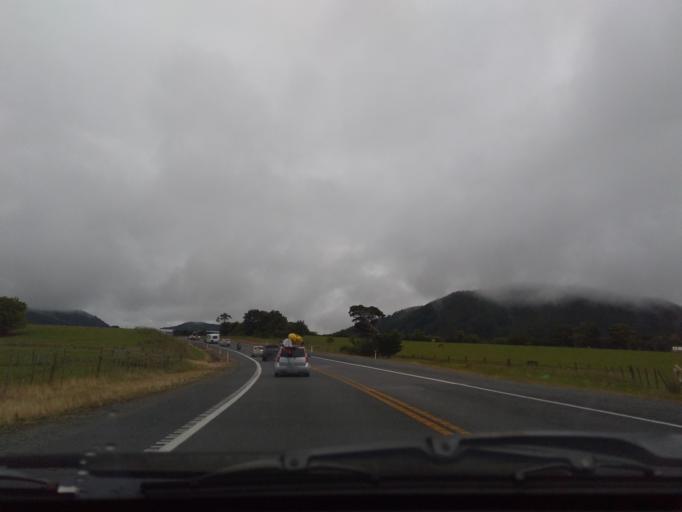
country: NZ
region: Auckland
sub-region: Auckland
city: Wellsford
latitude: -36.1462
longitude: 174.4381
